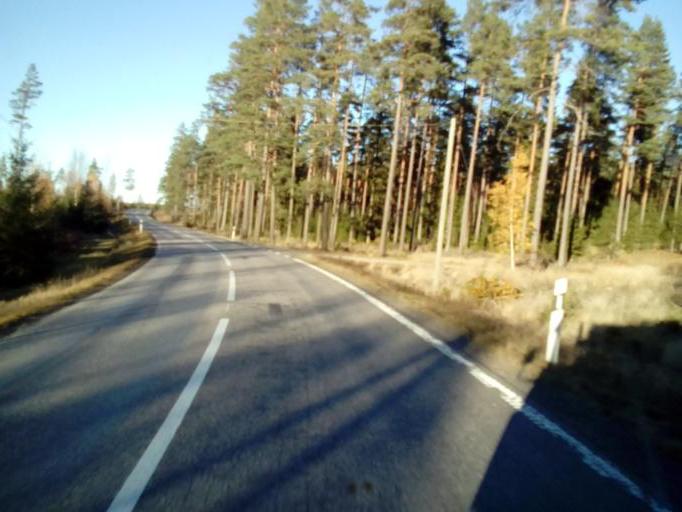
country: SE
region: OErebro
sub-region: Hallsbergs Kommun
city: Palsboda
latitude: 58.8566
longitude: 15.4073
